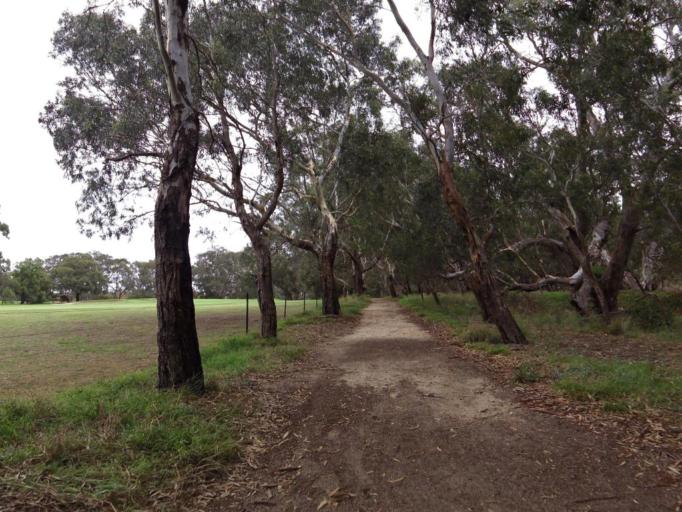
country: AU
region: Victoria
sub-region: Wyndham
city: Werribee
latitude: -37.9335
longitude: 144.6647
